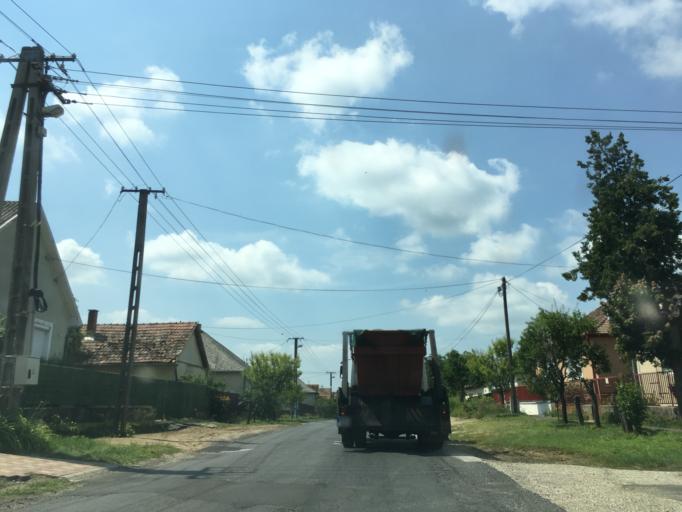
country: HU
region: Szabolcs-Szatmar-Bereg
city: Nyirlugos
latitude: 47.6571
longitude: 22.0363
